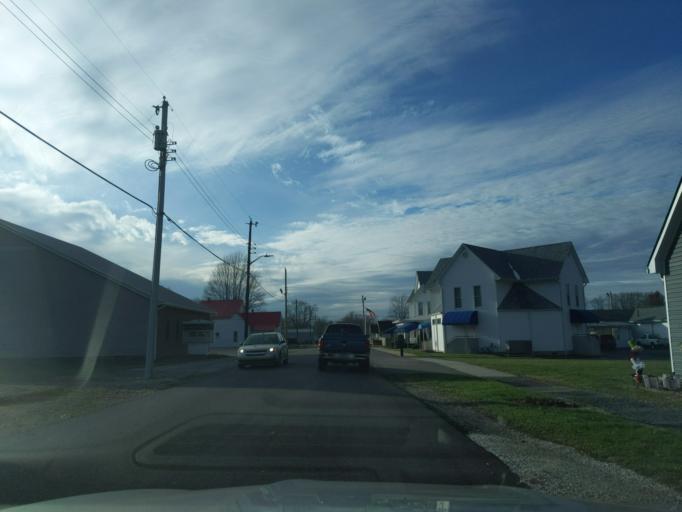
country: US
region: Indiana
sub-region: Decatur County
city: Westport
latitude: 39.1778
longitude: -85.5701
